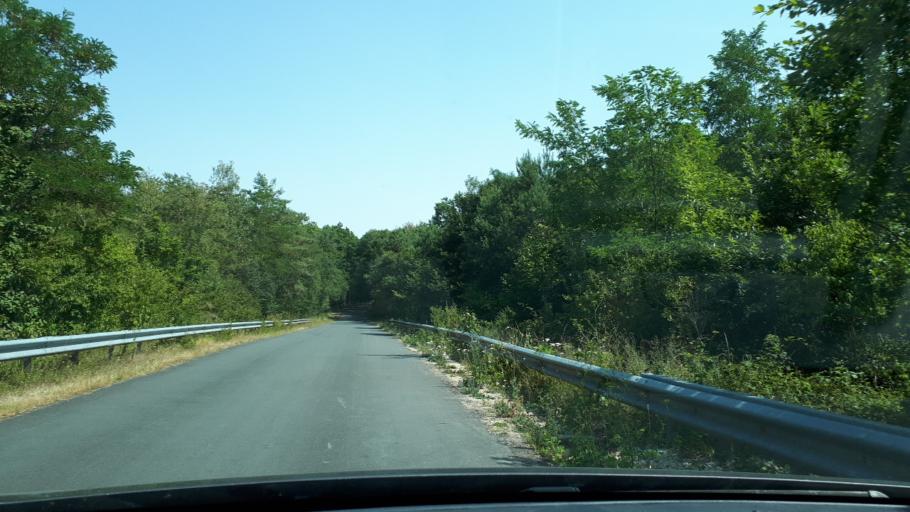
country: FR
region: Centre
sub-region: Departement du Loir-et-Cher
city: Aze
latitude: 47.8373
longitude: 1.0277
